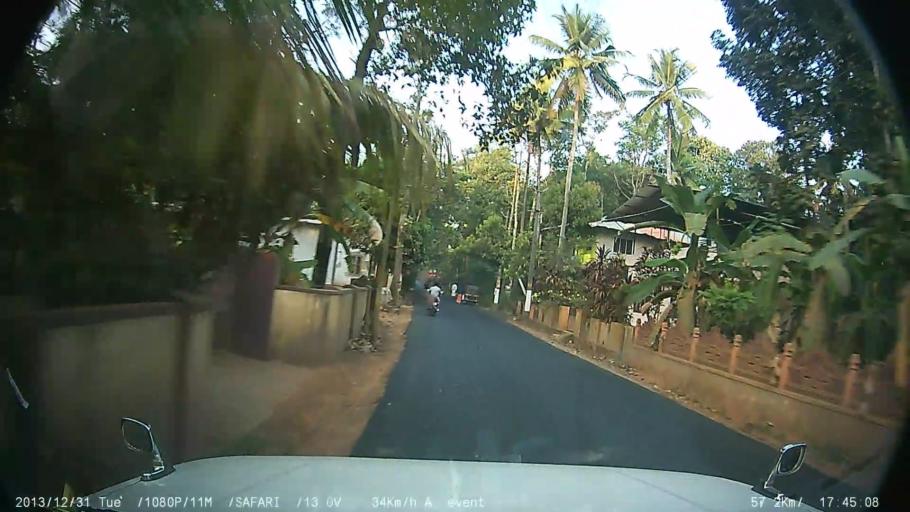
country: IN
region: Kerala
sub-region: Kottayam
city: Vaikam
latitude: 9.7291
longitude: 76.4779
